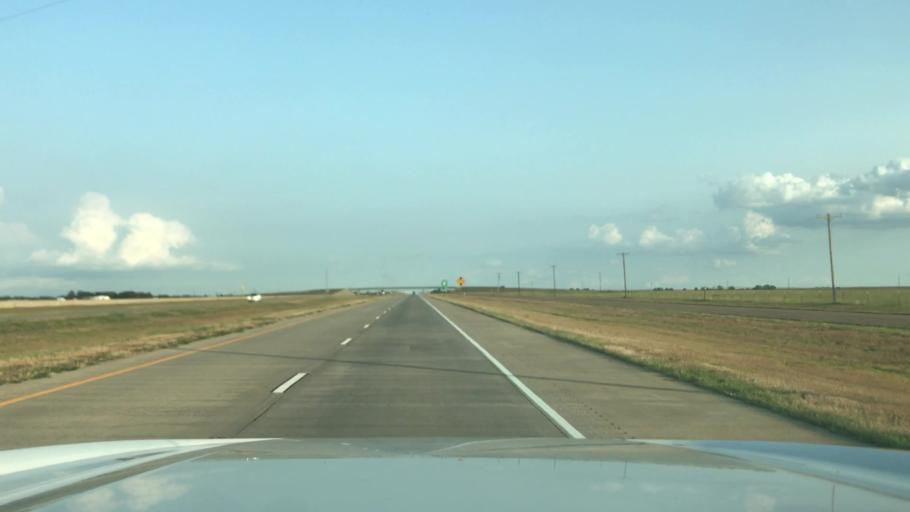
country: US
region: Texas
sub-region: Swisher County
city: Tulia
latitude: 34.3764
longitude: -101.7726
